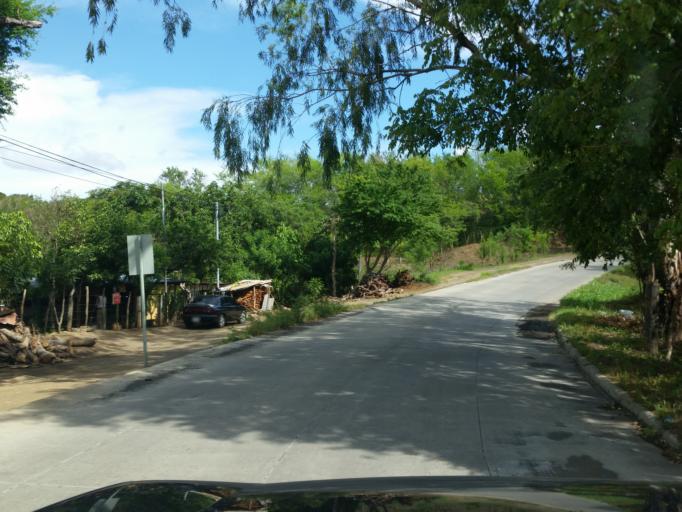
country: NI
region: Managua
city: Managua
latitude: 12.0821
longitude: -86.2448
